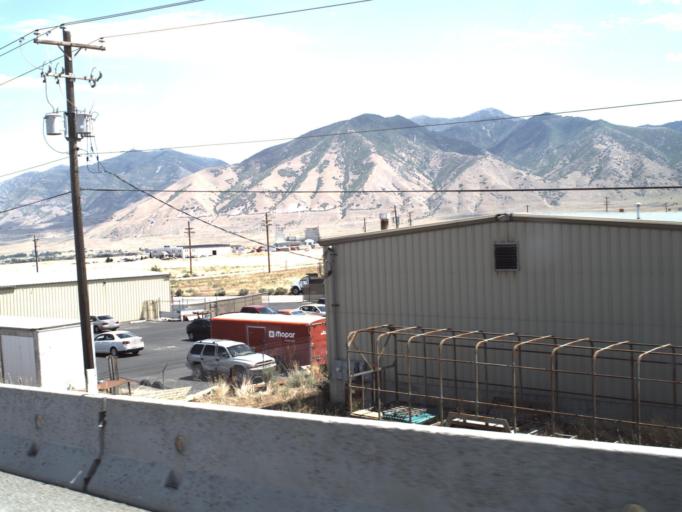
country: US
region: Utah
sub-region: Tooele County
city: Tooele
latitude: 40.5612
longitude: -112.2964
